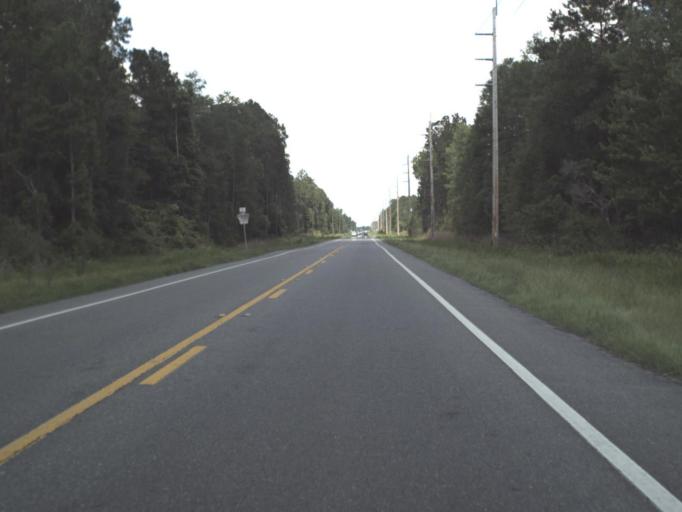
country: US
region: Florida
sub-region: Gilchrist County
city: Trenton
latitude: 29.6276
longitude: -82.7255
